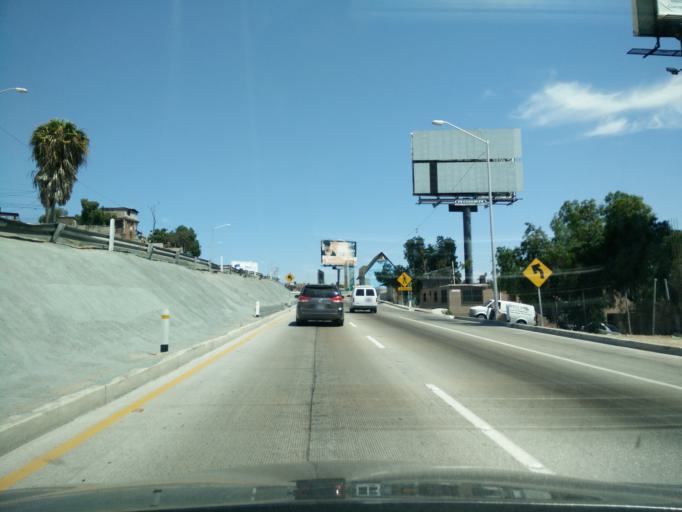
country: MX
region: Baja California
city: Tijuana
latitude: 32.5334
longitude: -117.0046
